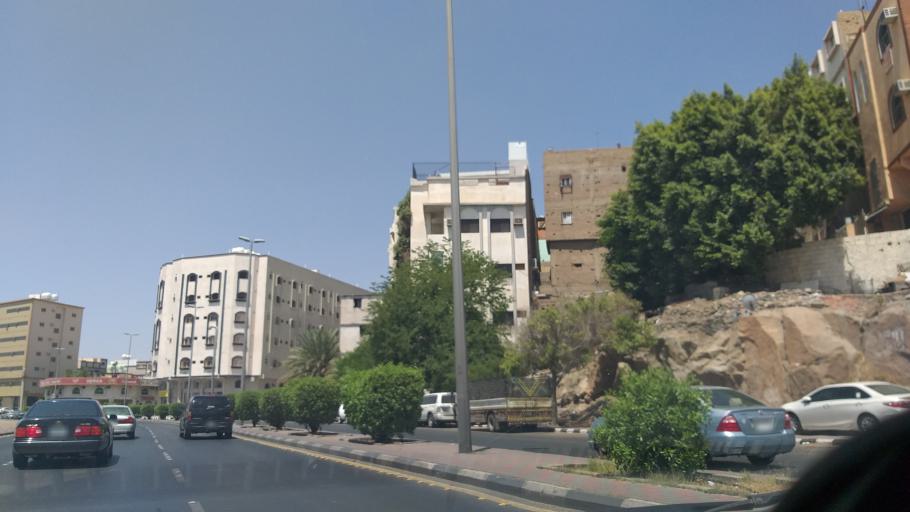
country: SA
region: Makkah
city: Ta'if
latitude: 21.2719
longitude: 40.4189
